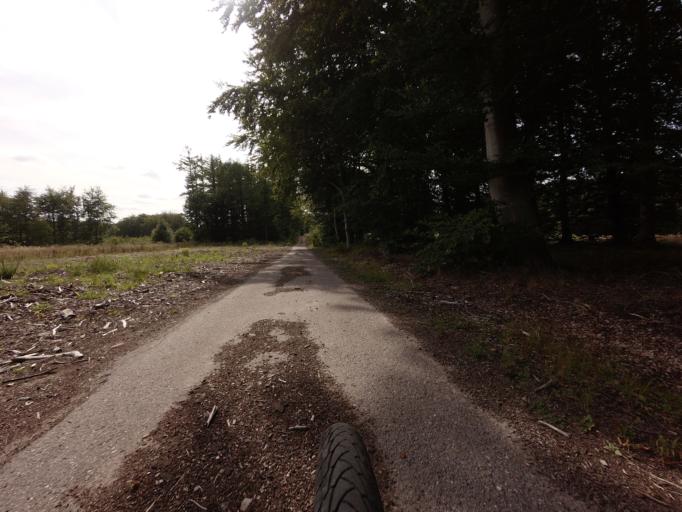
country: DK
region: Zealand
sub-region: Faxe Kommune
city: Fakse Ladeplads
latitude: 55.2338
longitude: 12.1906
